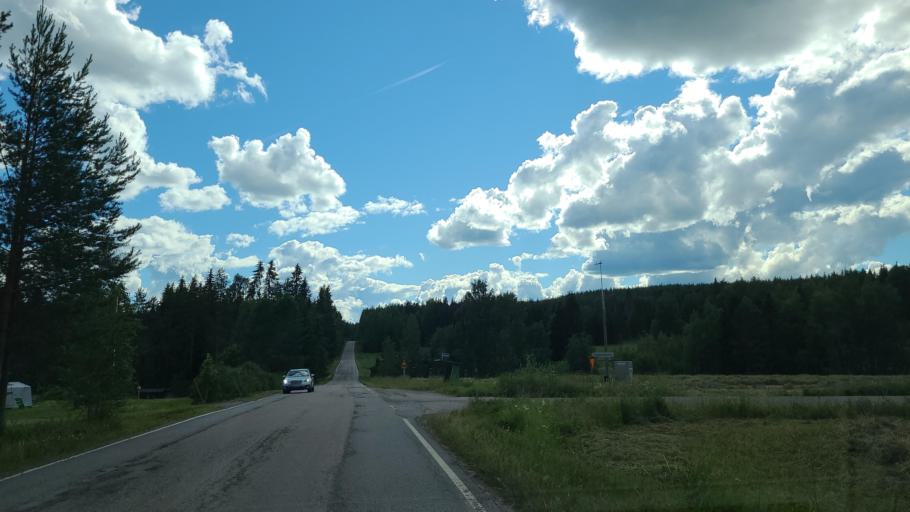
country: FI
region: Central Finland
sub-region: Jaemsae
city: Jaemsae
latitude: 61.8937
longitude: 25.2586
